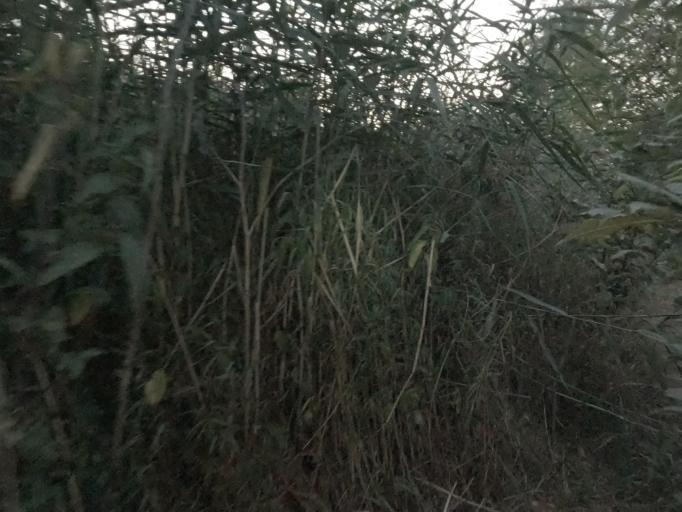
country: RU
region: St.-Petersburg
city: Avtovo
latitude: 59.8731
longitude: 30.2833
